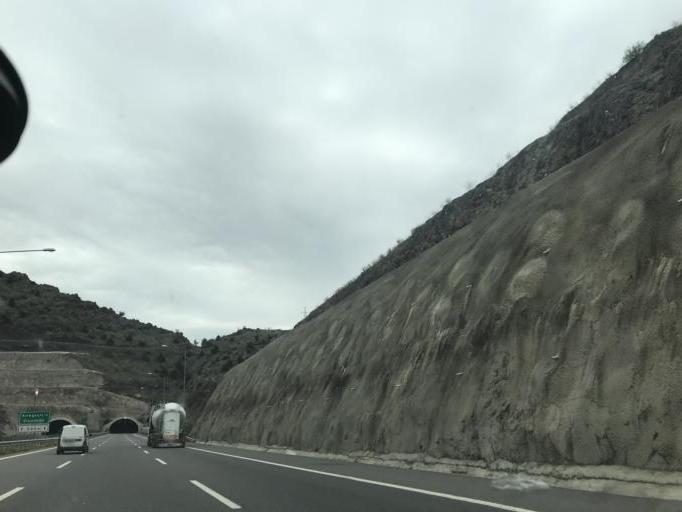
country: TR
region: Nigde
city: Ciftehan
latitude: 37.5562
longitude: 34.7680
